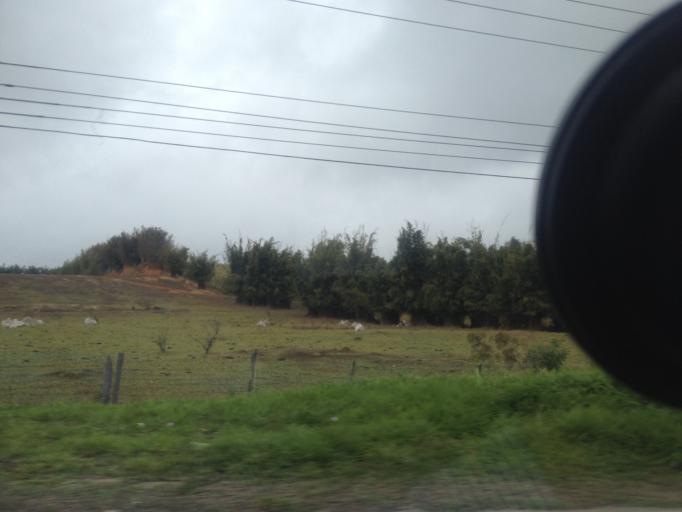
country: BR
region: Rio de Janeiro
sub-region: Porto Real
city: Porto Real
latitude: -22.4124
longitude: -44.3171
